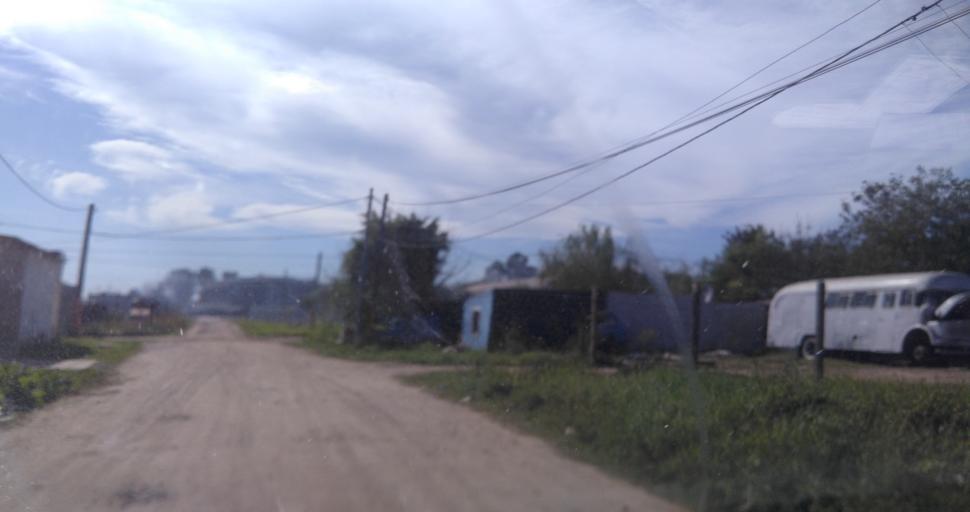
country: AR
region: Chaco
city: Fontana
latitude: -27.4349
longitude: -59.0218
